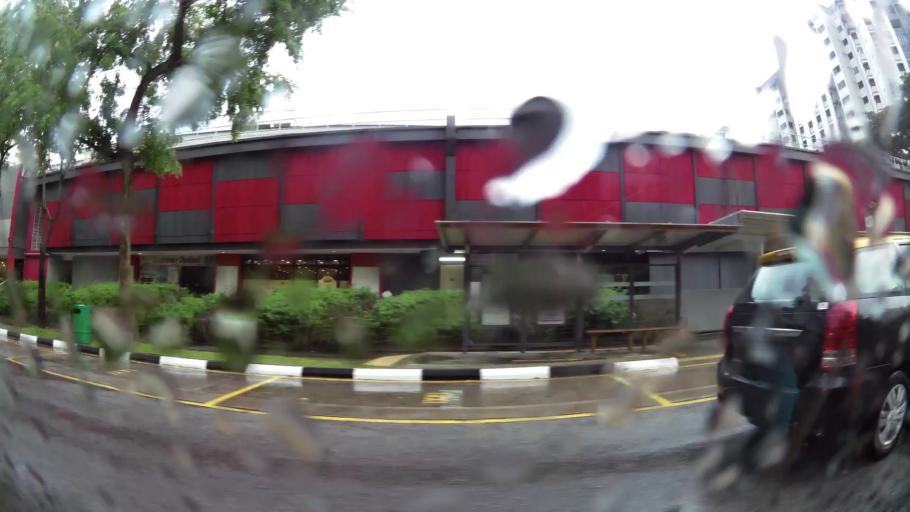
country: MY
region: Johor
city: Kampung Pasir Gudang Baru
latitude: 1.3854
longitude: 103.9012
